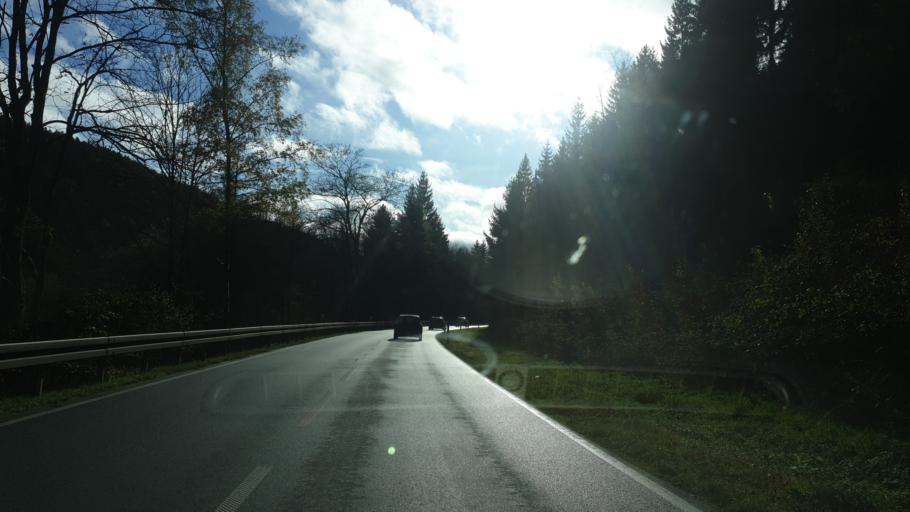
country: DE
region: Saxony
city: Zschorlau
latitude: 50.5403
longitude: 12.6554
